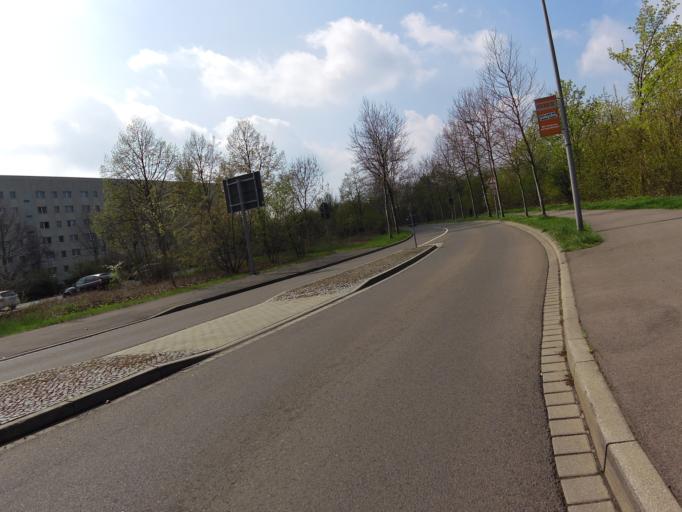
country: DE
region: Saxony
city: Markranstadt
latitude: 51.3263
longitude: 12.2649
